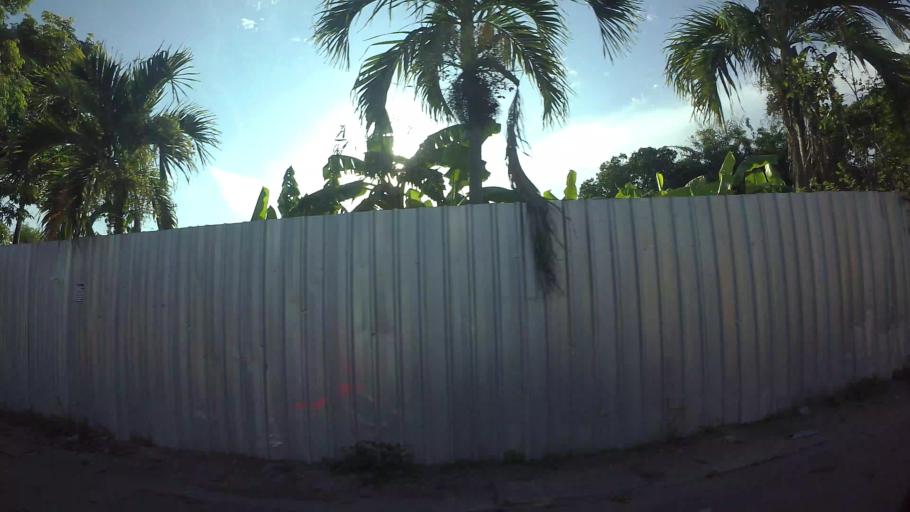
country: TH
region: Rayong
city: Rayong
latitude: 12.6835
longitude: 101.2882
